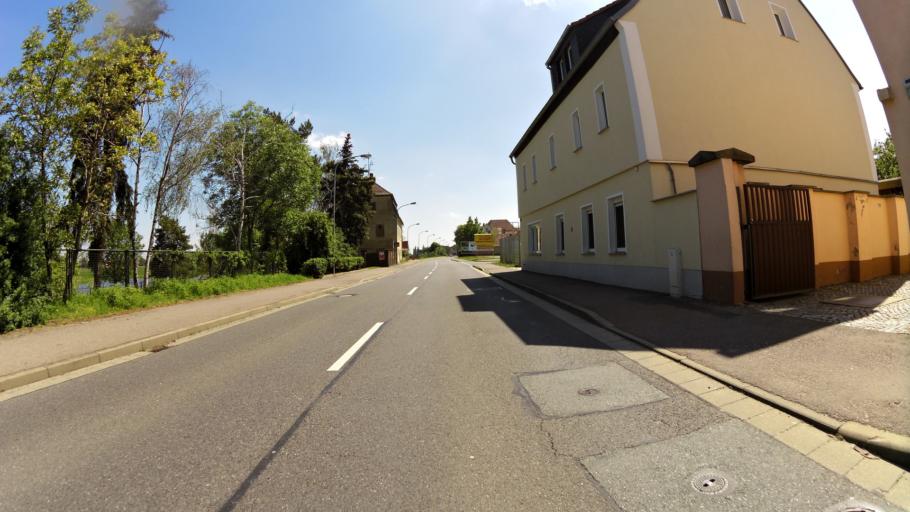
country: DE
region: Saxony
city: Strehla
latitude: 51.3507
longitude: 13.2386
